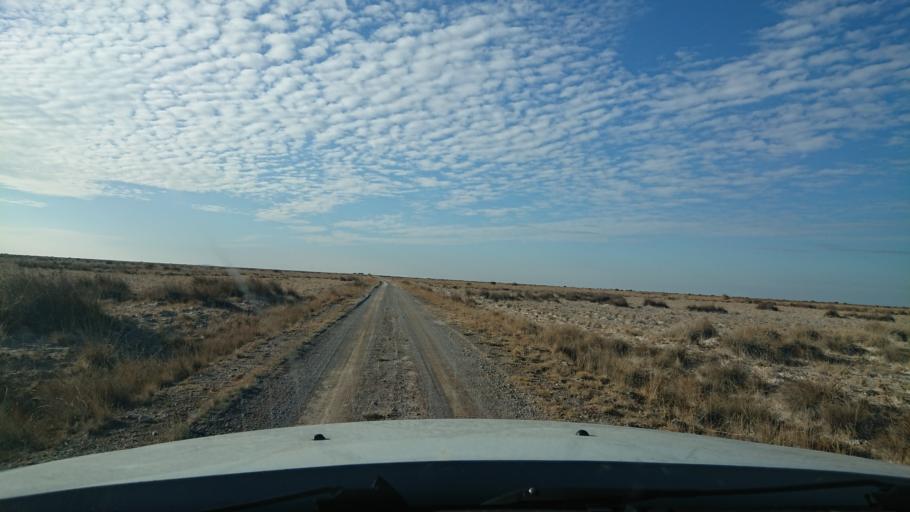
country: TR
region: Aksaray
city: Eskil
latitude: 38.5418
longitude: 33.3342
